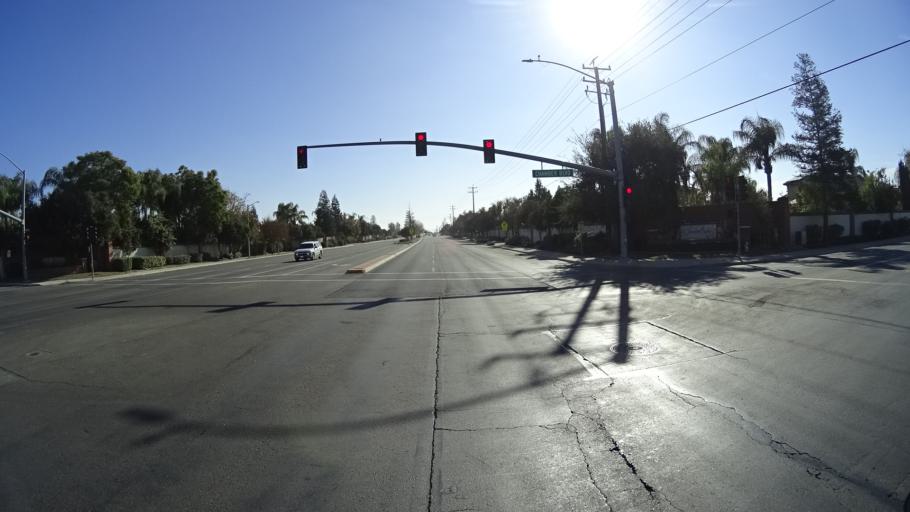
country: US
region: California
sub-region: Kern County
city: Rosedale
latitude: 35.3310
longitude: -119.1280
